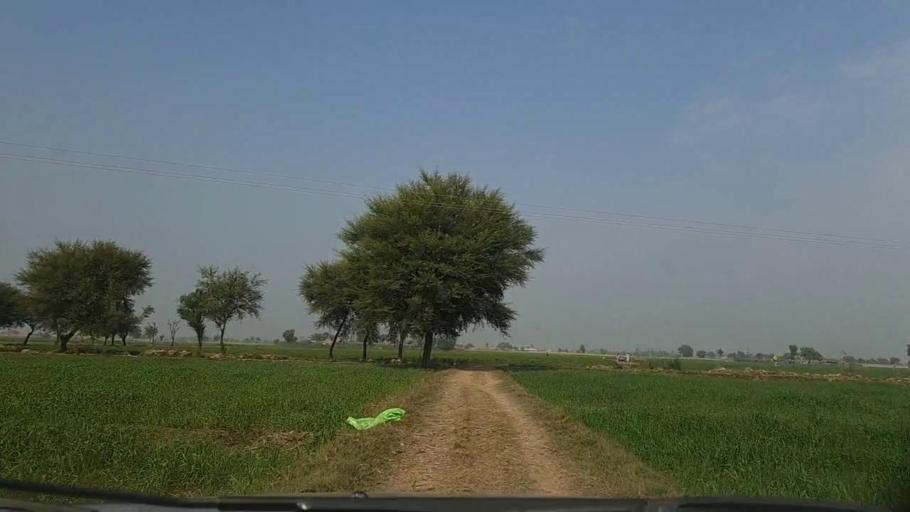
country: PK
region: Sindh
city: Sanghar
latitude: 26.0451
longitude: 68.9749
